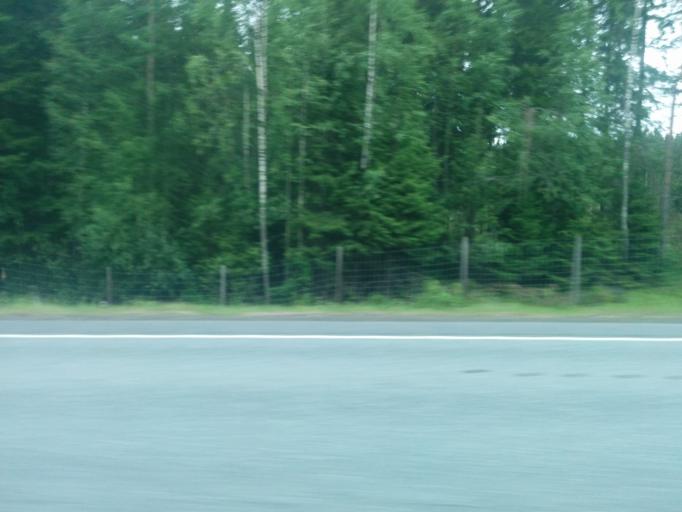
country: FI
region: Pirkanmaa
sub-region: Tampere
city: Orivesi
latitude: 61.6612
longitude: 24.2602
